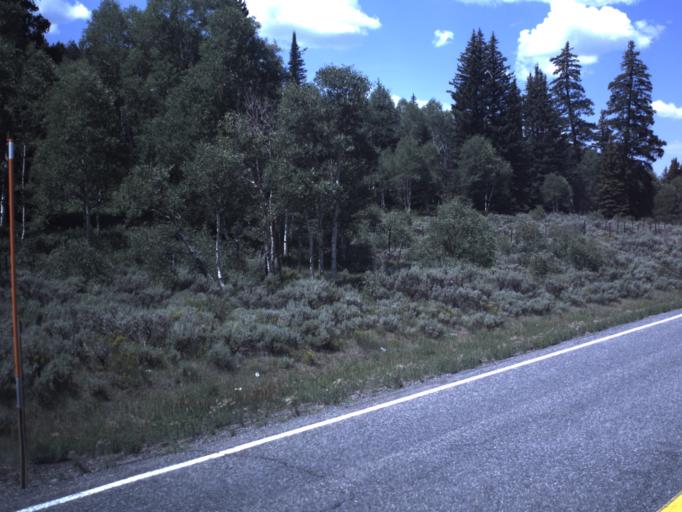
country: US
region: Utah
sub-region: Carbon County
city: Helper
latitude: 39.8609
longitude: -111.1093
